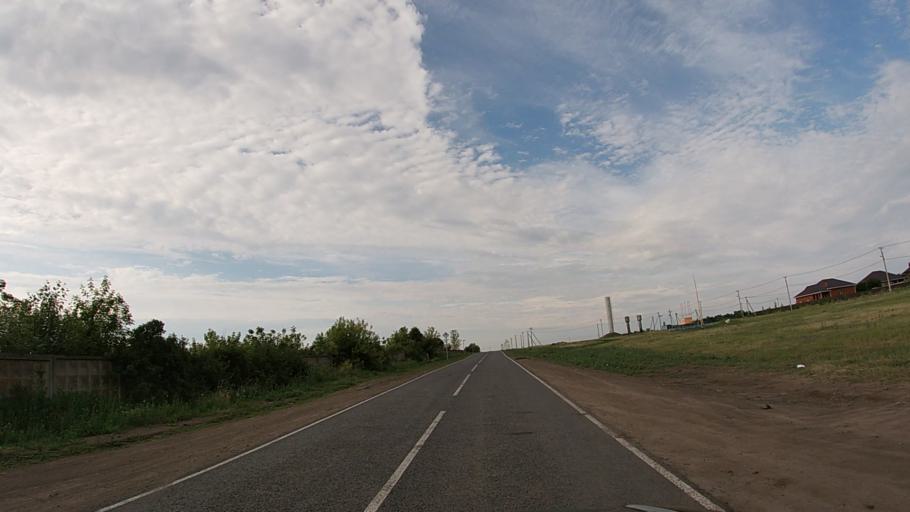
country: RU
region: Belgorod
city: Severnyy
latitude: 50.7258
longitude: 36.5846
